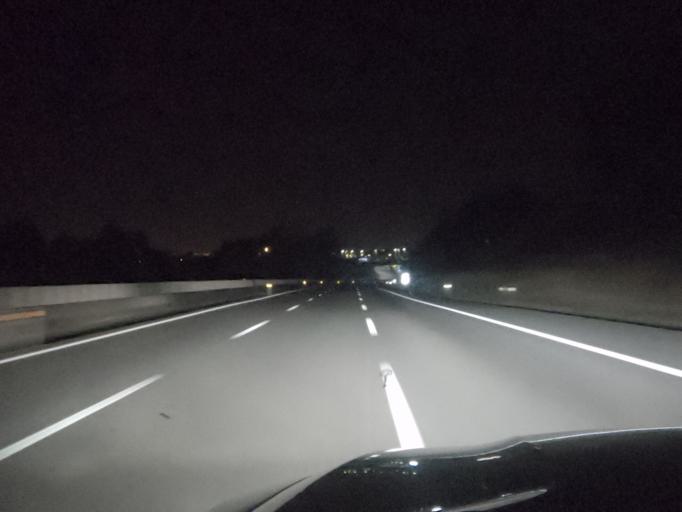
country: PT
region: Aveiro
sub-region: Santa Maria da Feira
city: Nogueira da Regedoura
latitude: 40.9986
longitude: -8.5835
